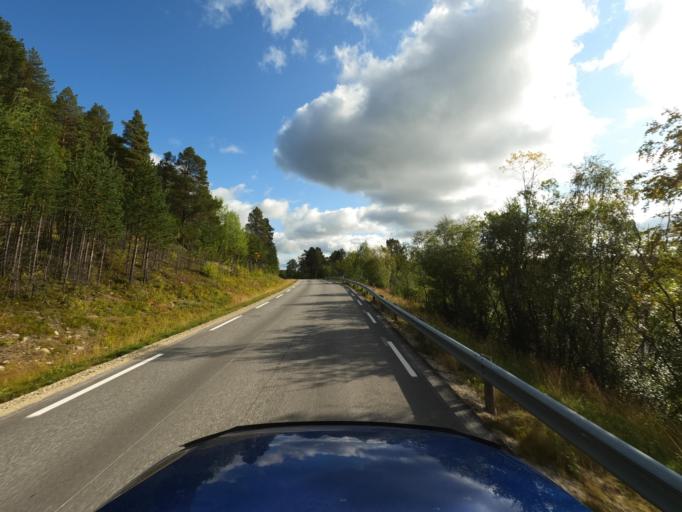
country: NO
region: Finnmark Fylke
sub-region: Karasjok
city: Karasjohka
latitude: 69.4292
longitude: 25.1052
